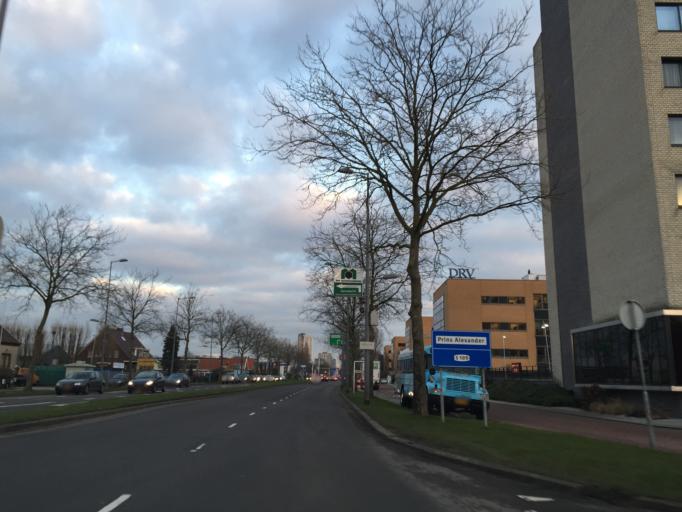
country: NL
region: South Holland
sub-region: Gemeente Rotterdam
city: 's-Gravenland
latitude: 51.9460
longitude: 4.5345
